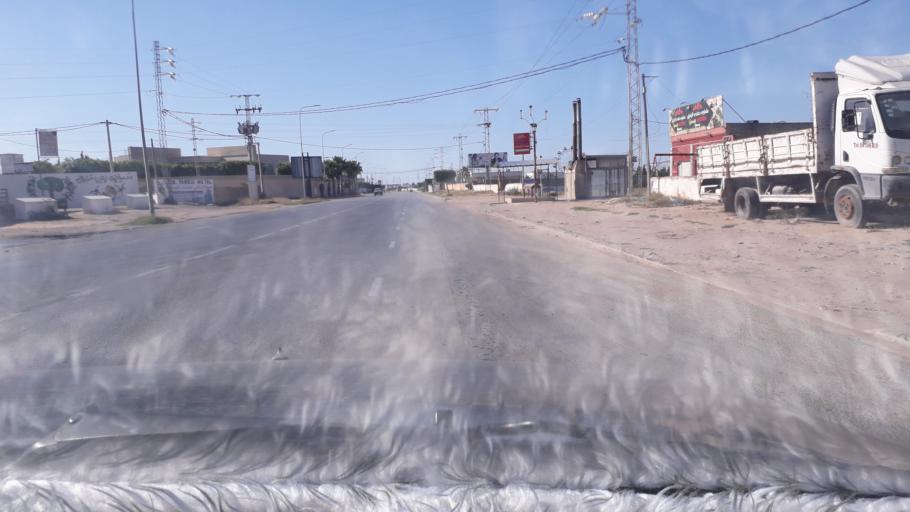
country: TN
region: Safaqis
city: Al Qarmadah
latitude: 34.8478
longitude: 10.7619
